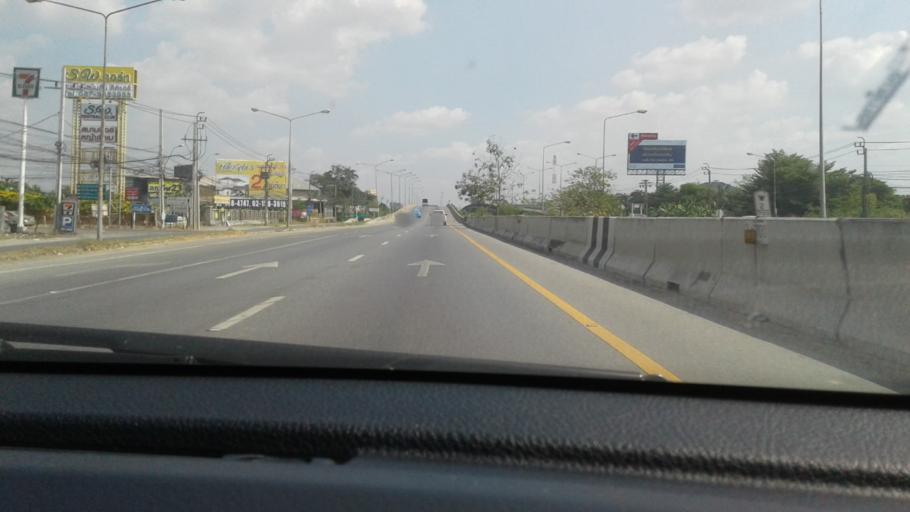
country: TH
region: Nonthaburi
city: Bang Bua Thong
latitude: 13.9478
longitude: 100.4416
